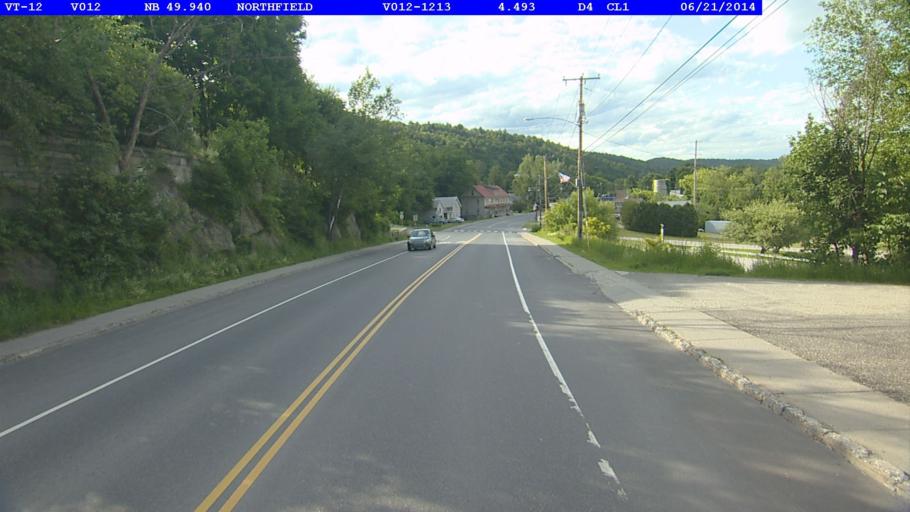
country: US
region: Vermont
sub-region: Washington County
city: Northfield
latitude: 44.1532
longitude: -72.6561
